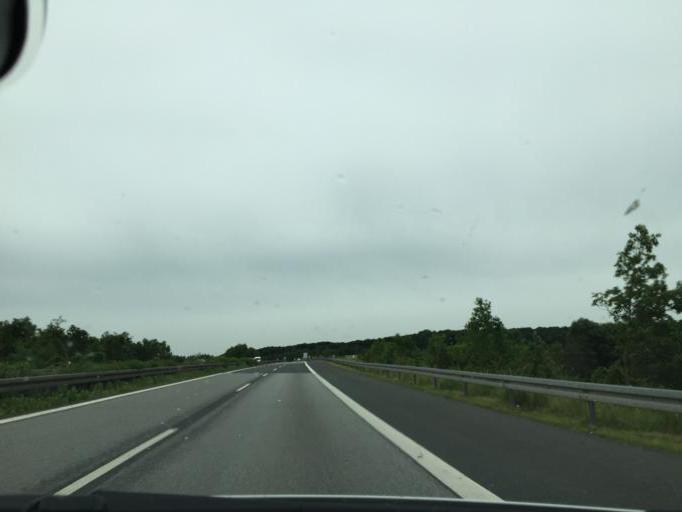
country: DE
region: Bavaria
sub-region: Regierungsbezirk Unterfranken
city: Gadheim
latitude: 50.0156
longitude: 10.3400
